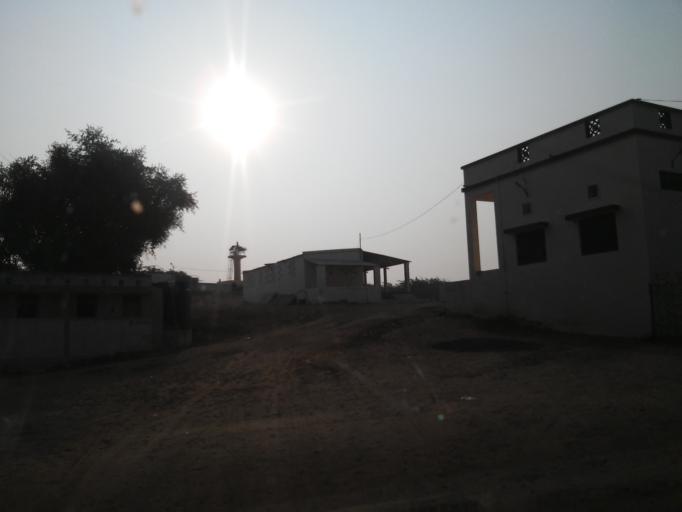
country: IN
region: Gujarat
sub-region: Kachchh
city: Mandvi
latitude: 22.8153
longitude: 69.3908
